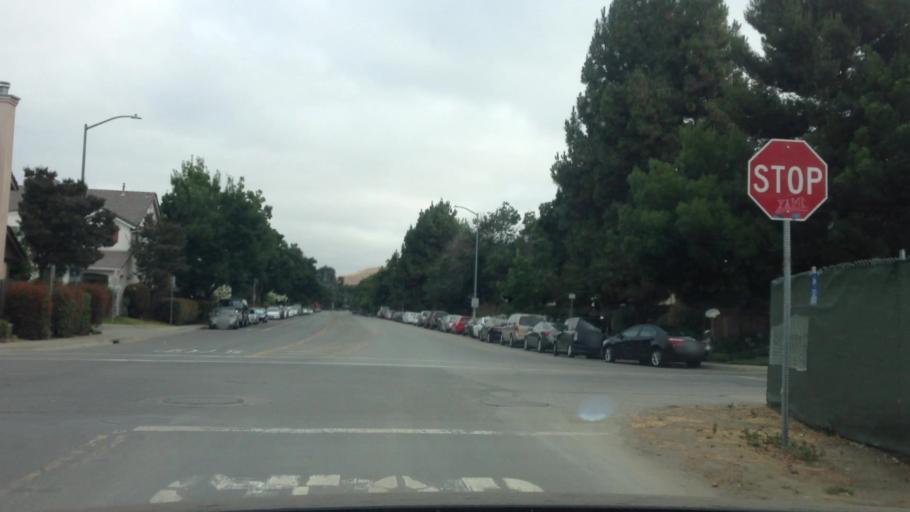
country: US
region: California
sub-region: Alameda County
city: Fremont
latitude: 37.5615
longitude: -121.9725
